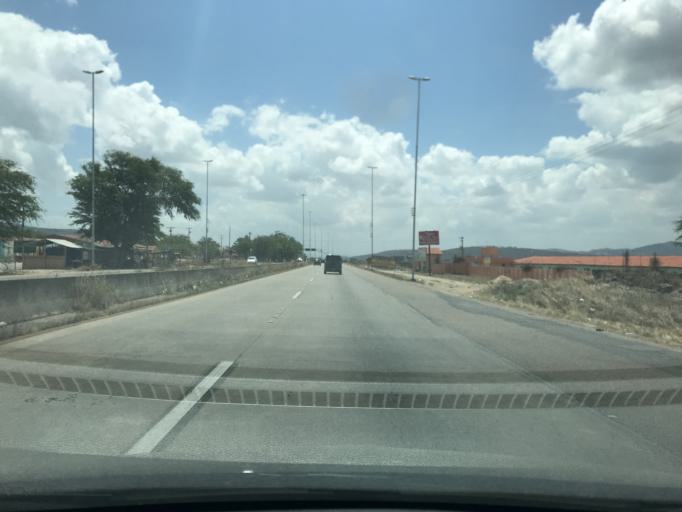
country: BR
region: Pernambuco
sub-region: Bezerros
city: Bezerros
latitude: -8.3001
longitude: -35.8500
